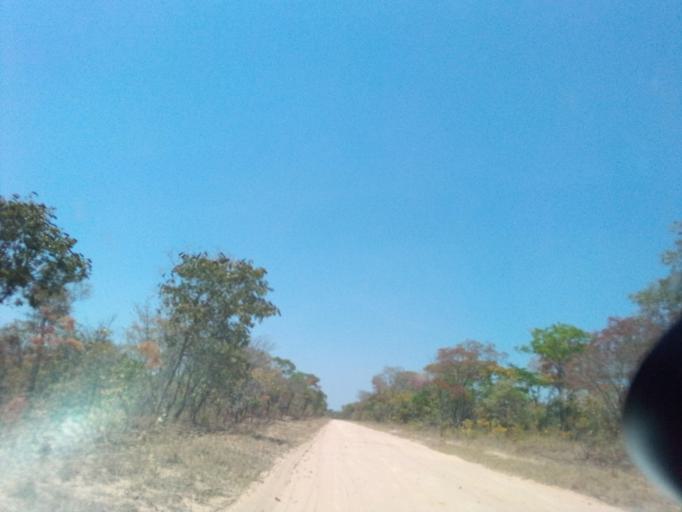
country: ZM
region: Northern
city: Mpika
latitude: -12.2363
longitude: 30.6595
